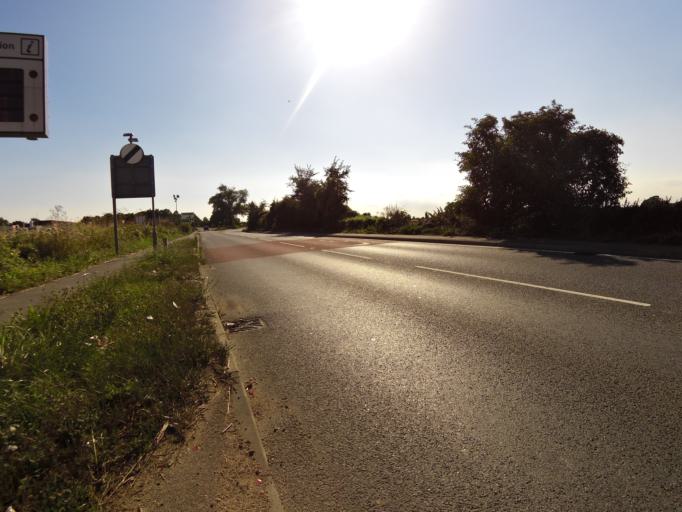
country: GB
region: England
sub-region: Essex
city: Witham
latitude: 51.7865
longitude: 0.6203
